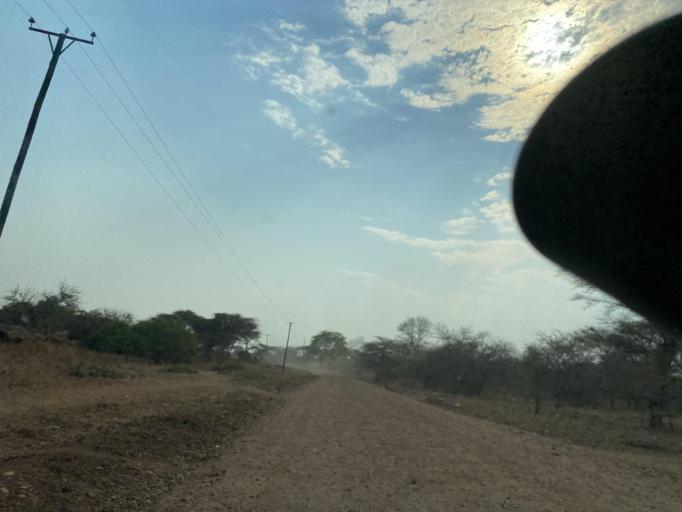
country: ZW
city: Chirundu
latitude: -15.9194
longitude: 28.9776
